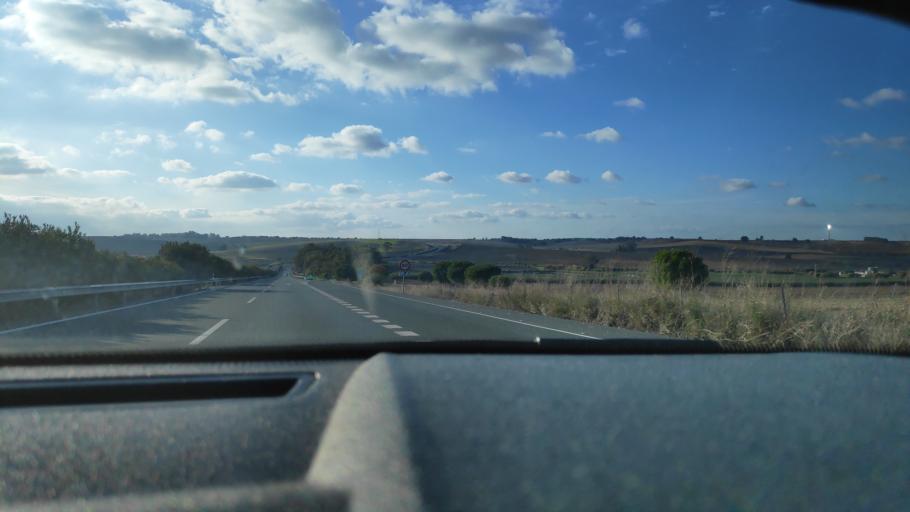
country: ES
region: Andalusia
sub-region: Provincia de Sevilla
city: La Luisiana
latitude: 37.5273
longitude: -5.2751
